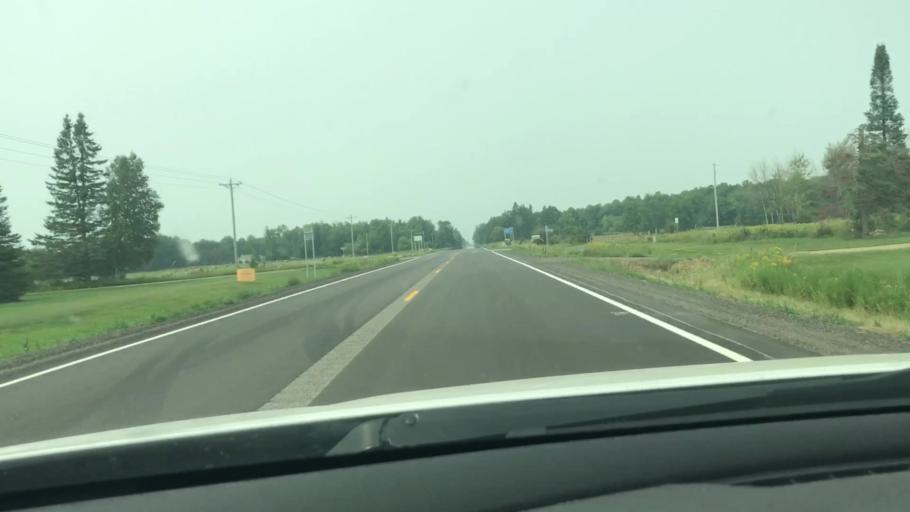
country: US
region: Minnesota
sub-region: Itasca County
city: Cohasset
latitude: 47.3545
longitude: -93.8480
